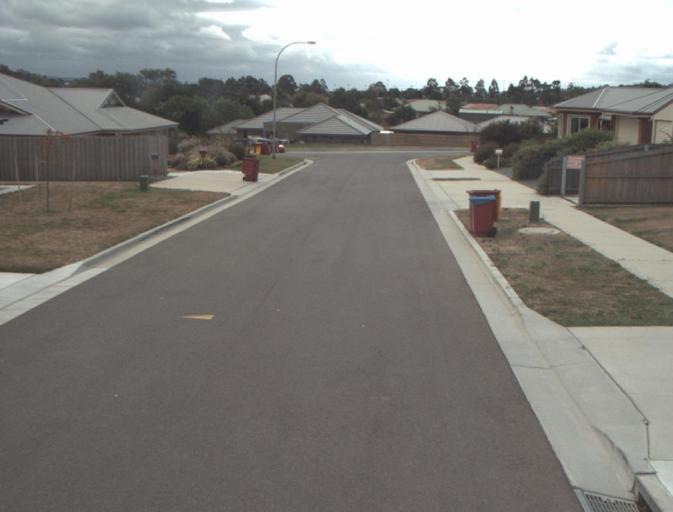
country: AU
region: Tasmania
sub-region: Launceston
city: Newstead
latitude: -41.4595
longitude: 147.1978
